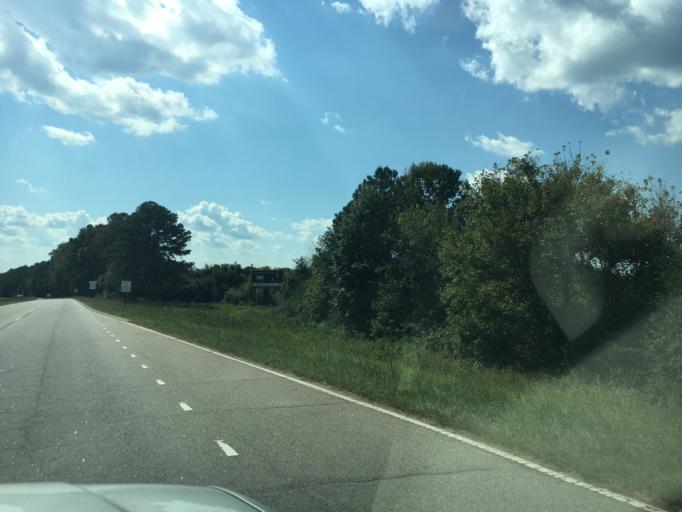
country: US
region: South Carolina
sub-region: Pickens County
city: Liberty
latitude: 34.7509
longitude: -82.7075
